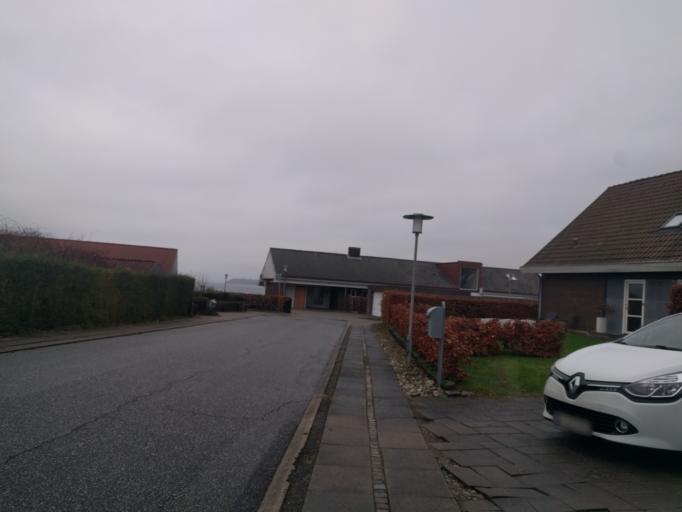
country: DK
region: South Denmark
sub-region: Fredericia Kommune
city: Snoghoj
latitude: 55.5408
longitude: 9.7283
